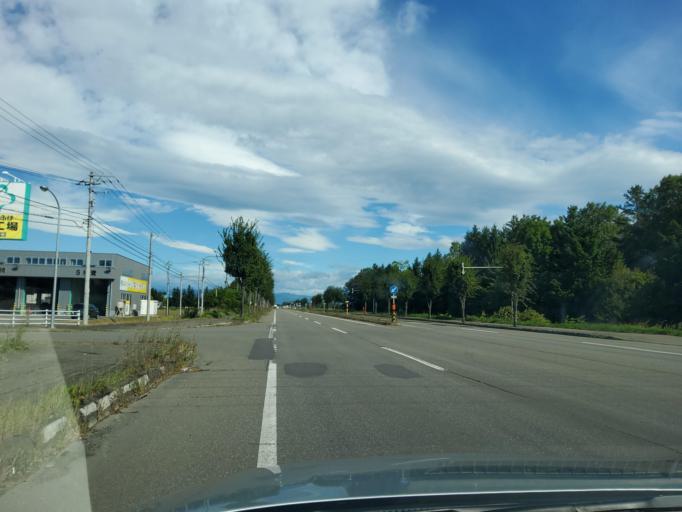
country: JP
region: Hokkaido
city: Otofuke
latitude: 42.9857
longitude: 143.1833
